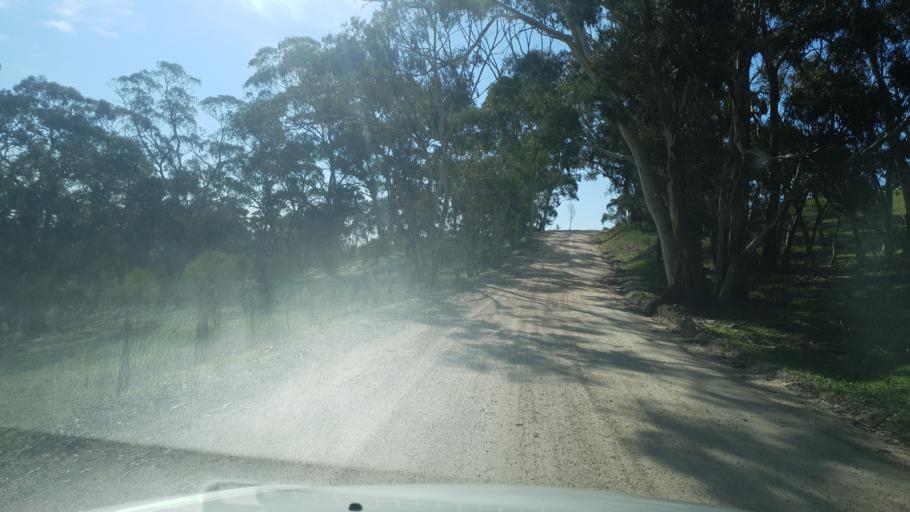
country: AU
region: South Australia
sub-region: Playford
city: One Tree Hill
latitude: -34.6537
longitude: 138.8174
